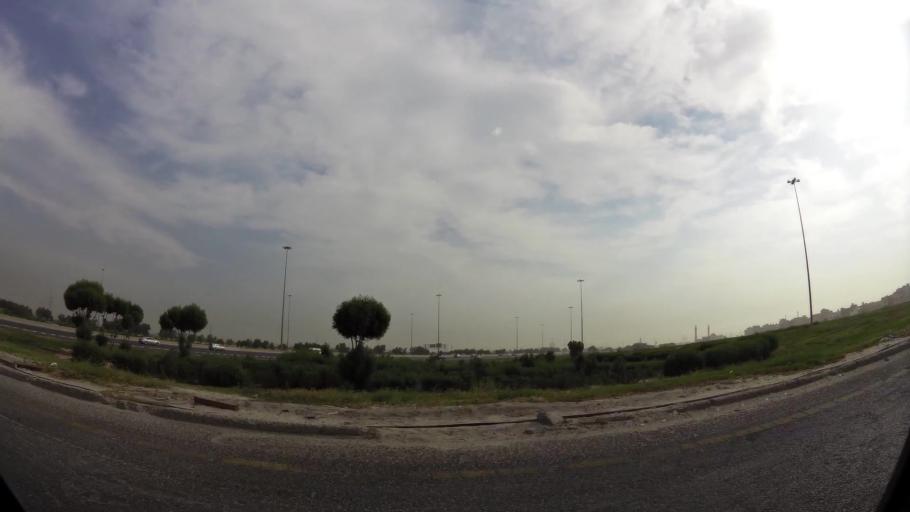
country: KW
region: Muhafazat al Jahra'
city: Al Jahra'
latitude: 29.3107
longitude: 47.7872
